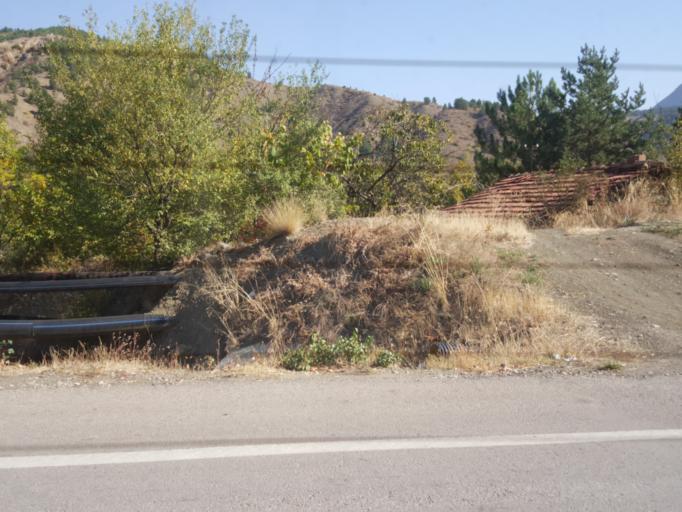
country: TR
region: Corum
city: Iskilip
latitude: 40.7377
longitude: 34.4526
